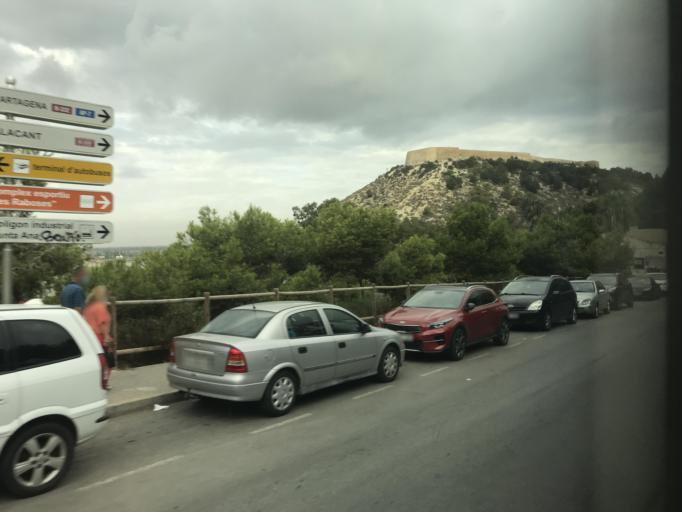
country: ES
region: Valencia
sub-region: Provincia de Alicante
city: Guardamar del Segura
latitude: 38.0884
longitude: -0.6559
